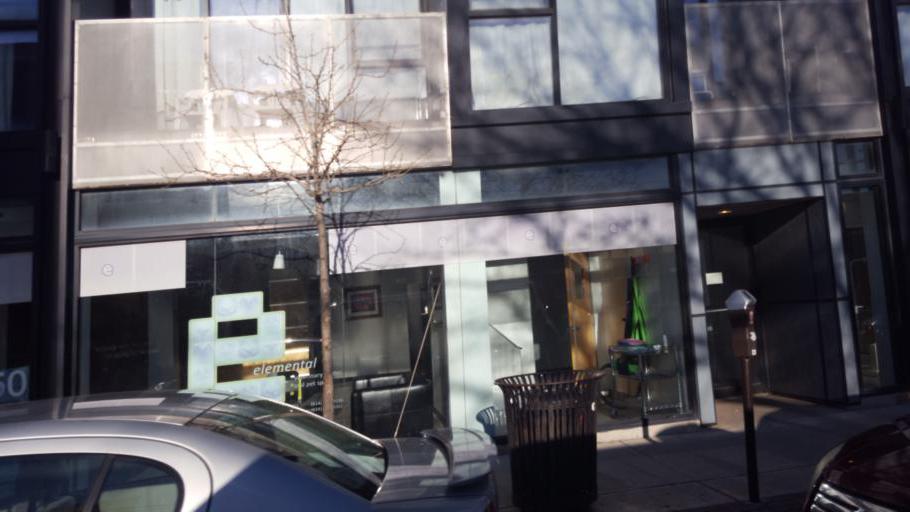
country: US
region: Ohio
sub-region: Franklin County
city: Columbus
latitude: 39.9879
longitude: -83.0057
